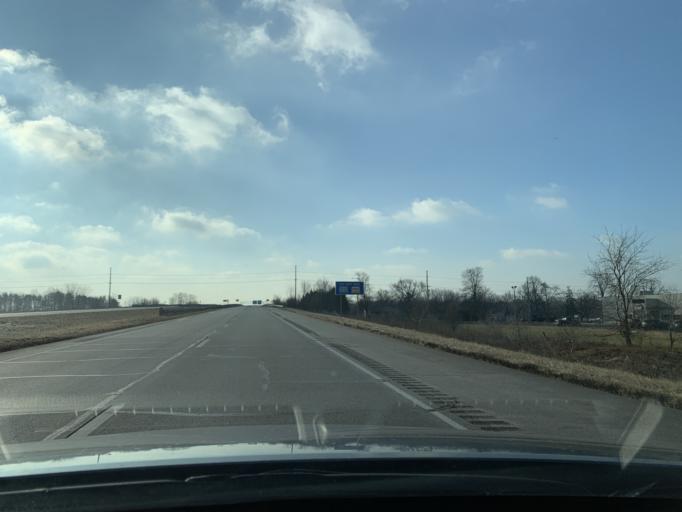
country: US
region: Indiana
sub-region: Porter County
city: Valparaiso
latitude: 41.4801
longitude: -87.0205
